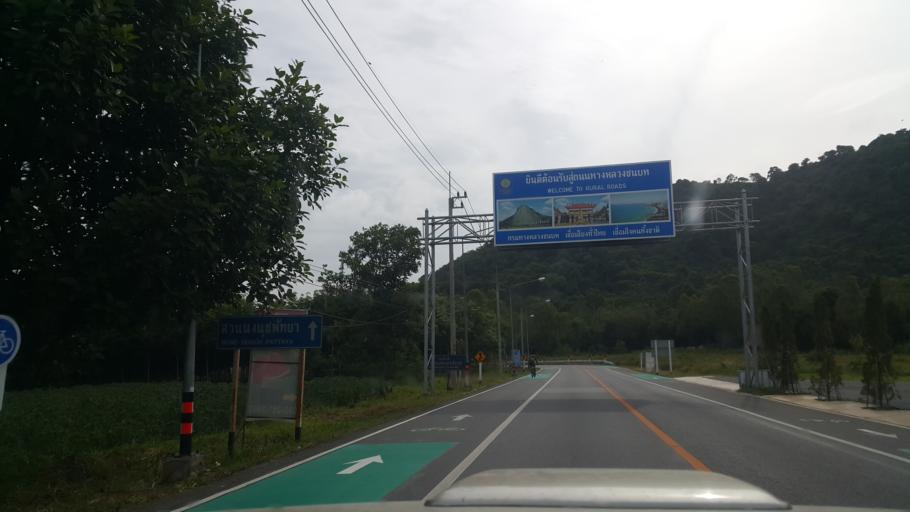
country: TH
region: Rayong
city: Ban Chang
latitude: 12.7636
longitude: 100.9904
